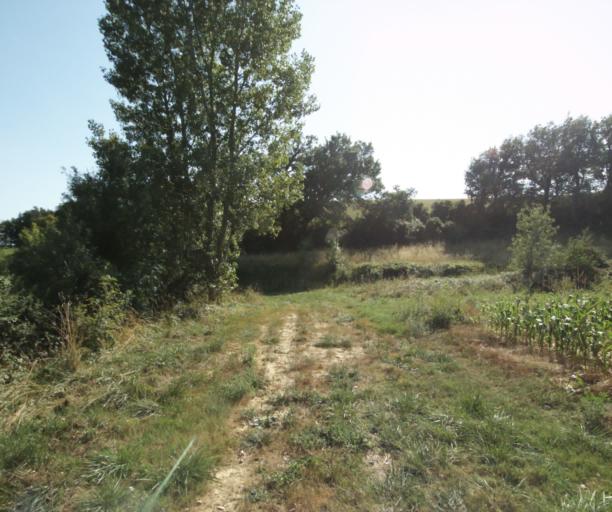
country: FR
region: Midi-Pyrenees
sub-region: Departement de la Haute-Garonne
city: Avignonet-Lauragais
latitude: 43.4238
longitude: 1.8252
